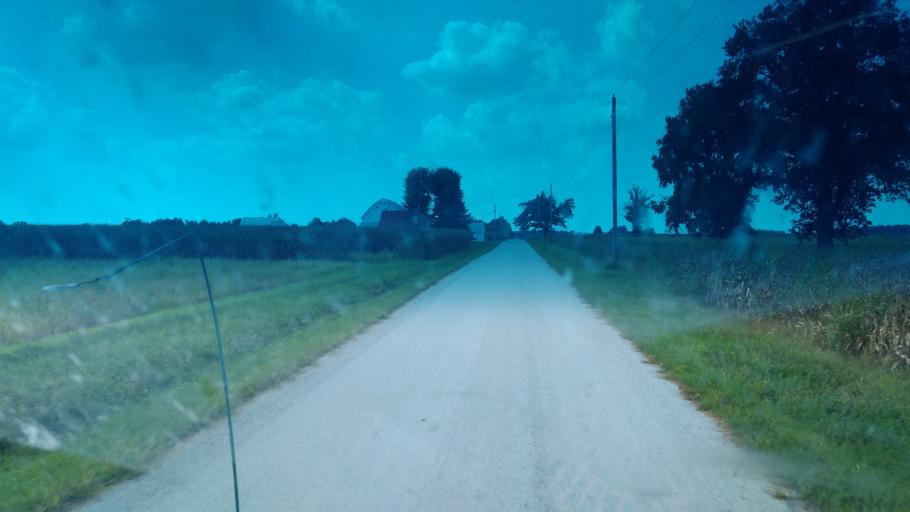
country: US
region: Ohio
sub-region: Hardin County
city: Kenton
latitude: 40.6893
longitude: -83.7175
